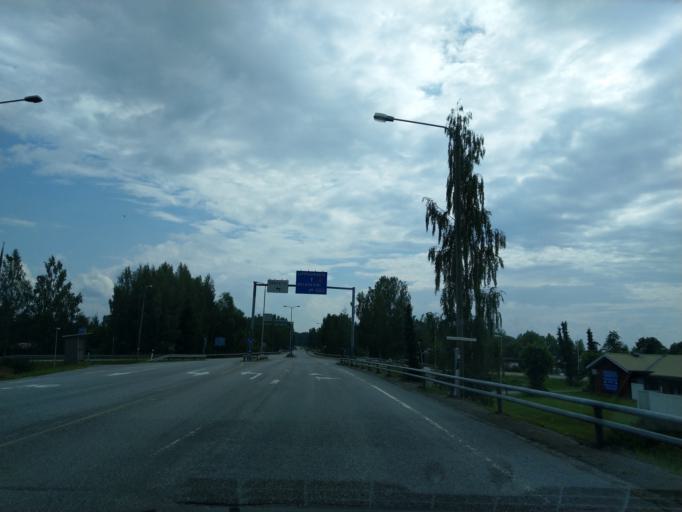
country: FI
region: South Karelia
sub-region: Imatra
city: Parikkala
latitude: 61.6025
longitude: 29.4824
